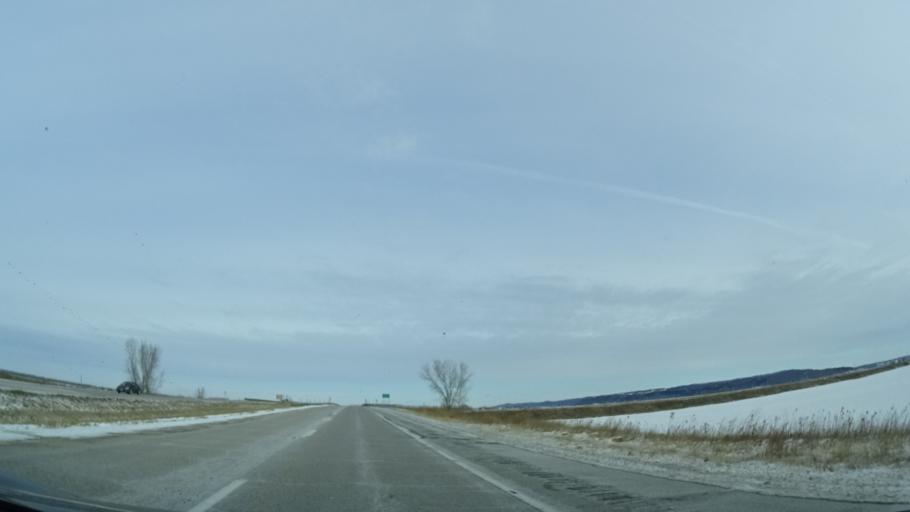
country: US
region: Nebraska
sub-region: Burt County
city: Tekamah
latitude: 41.7490
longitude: -96.0465
